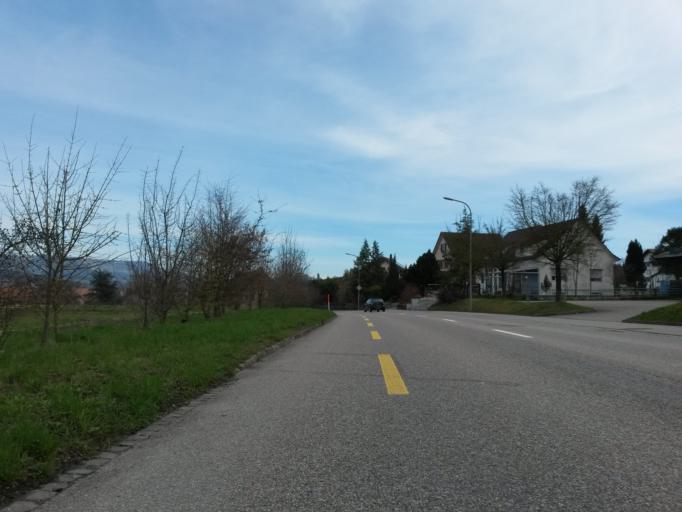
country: CH
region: Solothurn
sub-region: Bezirk Lebern
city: Langendorf
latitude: 47.1885
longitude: 7.4977
